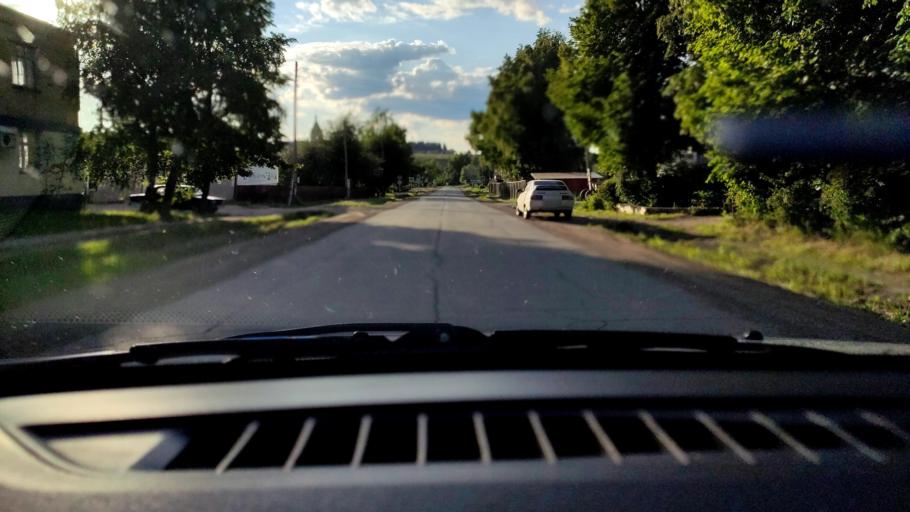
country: RU
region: Perm
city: Uinskoye
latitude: 57.1154
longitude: 56.5275
